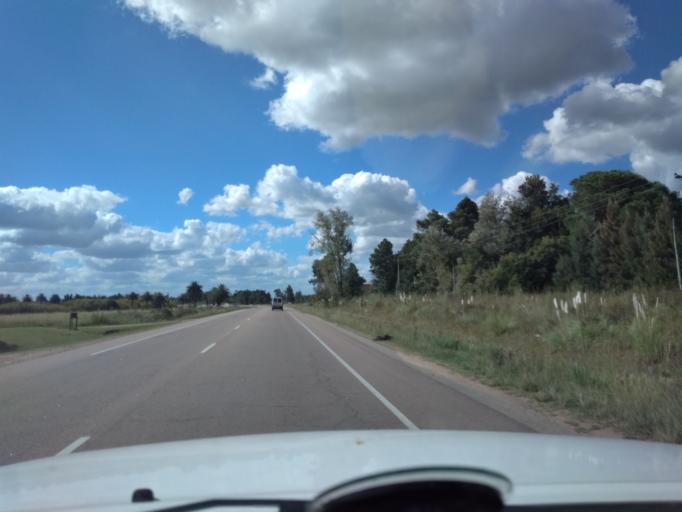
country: UY
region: Canelones
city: Sauce
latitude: -34.6792
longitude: -56.0519
